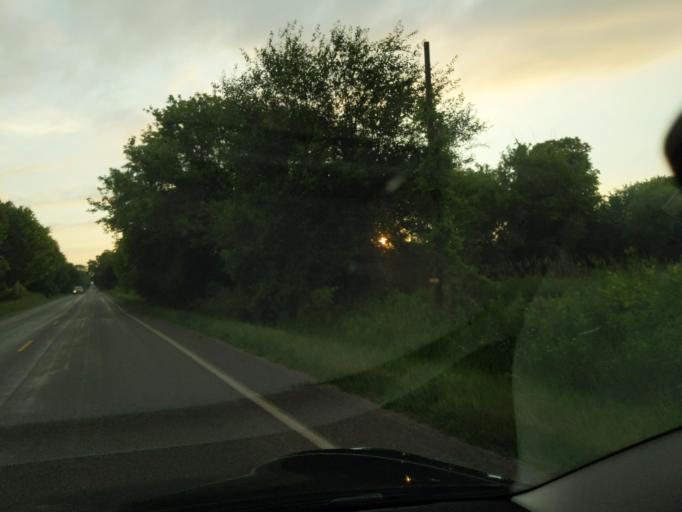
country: US
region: Michigan
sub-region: Ingham County
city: Mason
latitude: 42.5239
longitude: -84.4047
